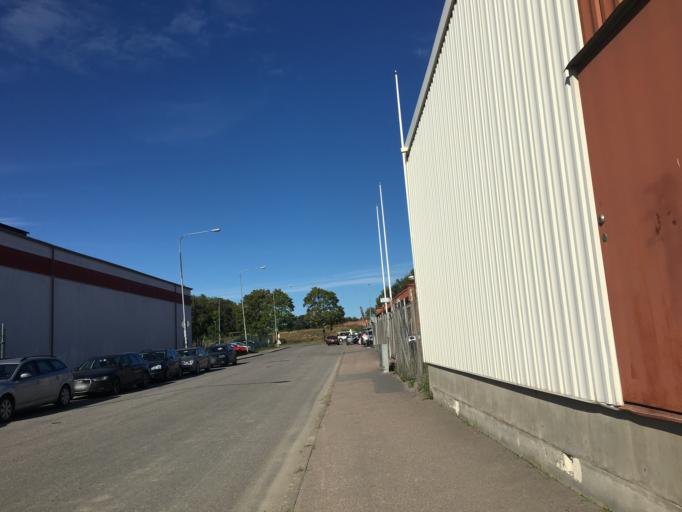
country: SE
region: Uppsala
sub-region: Uppsala Kommun
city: Uppsala
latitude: 59.8536
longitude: 17.6706
